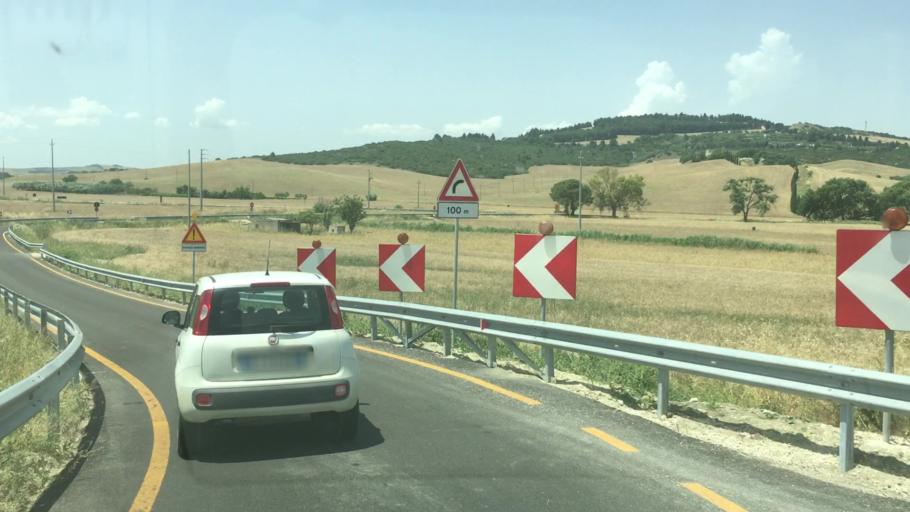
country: IT
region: Basilicate
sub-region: Provincia di Matera
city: La Martella
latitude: 40.6717
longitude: 16.4944
